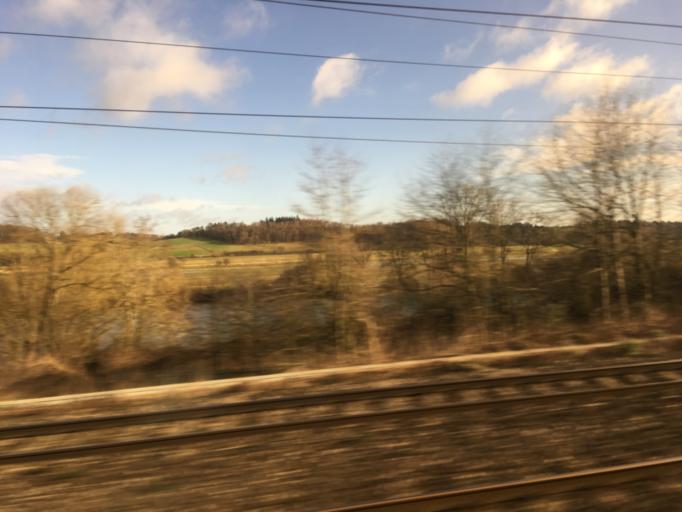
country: GB
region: England
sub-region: West Berkshire
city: Tilehurst
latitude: 51.4709
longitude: -1.0283
